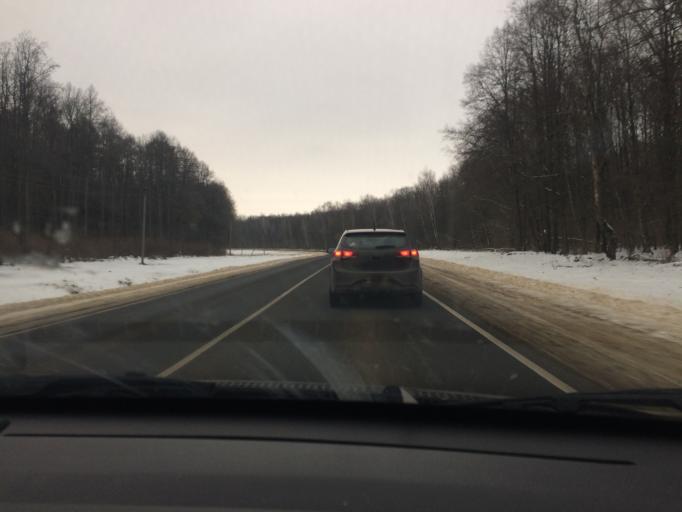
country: RU
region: Tula
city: Venev
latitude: 54.3355
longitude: 38.0971
